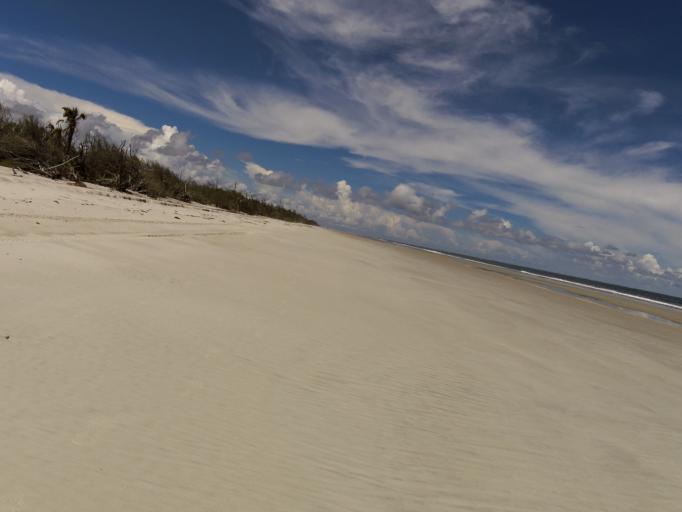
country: US
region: Florida
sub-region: Duval County
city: Atlantic Beach
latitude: 30.4703
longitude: -81.4125
